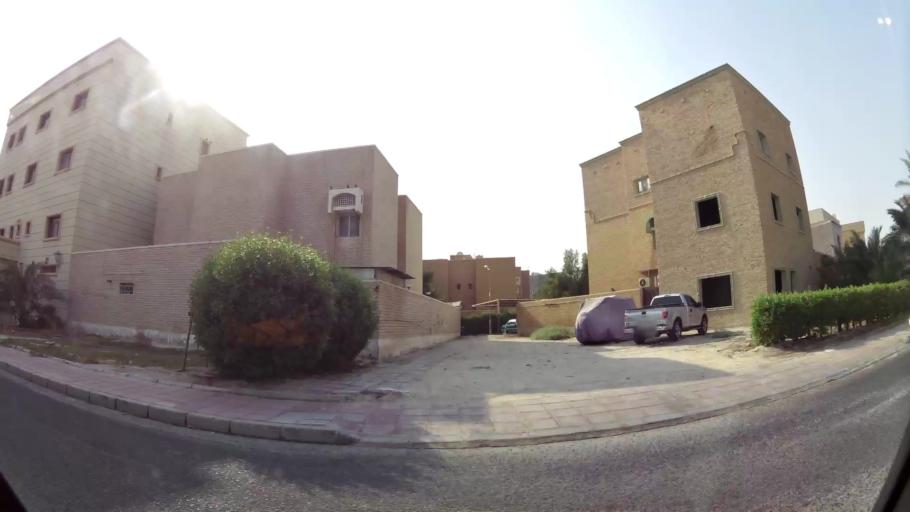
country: KW
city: Al Funaytis
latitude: 29.2179
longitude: 48.0833
